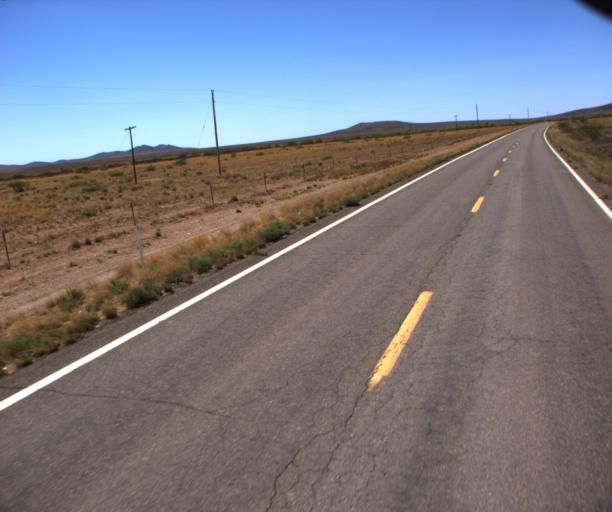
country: US
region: Arizona
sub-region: Cochise County
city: Douglas
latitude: 31.6552
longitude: -109.1575
